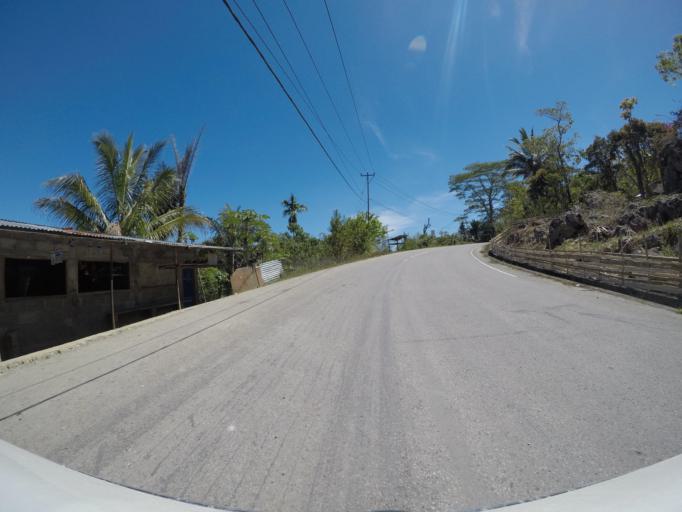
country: TL
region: Manatuto
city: Manatuto
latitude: -8.7920
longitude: 125.9698
